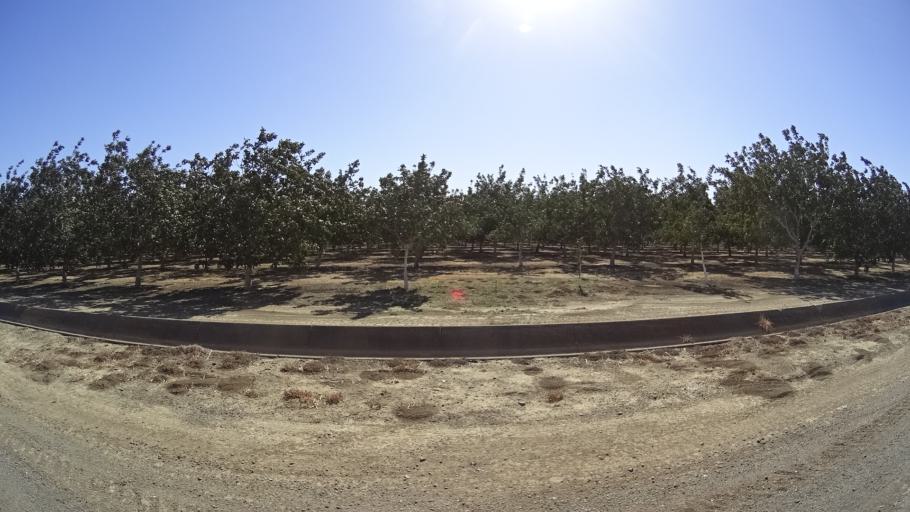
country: US
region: California
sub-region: Yolo County
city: Winters
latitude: 38.5841
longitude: -121.9677
